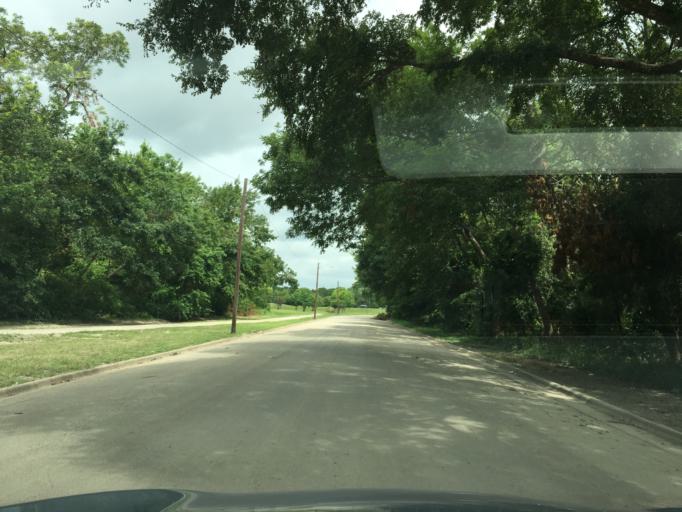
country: US
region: Texas
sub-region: Dallas County
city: University Park
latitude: 32.8790
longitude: -96.7463
